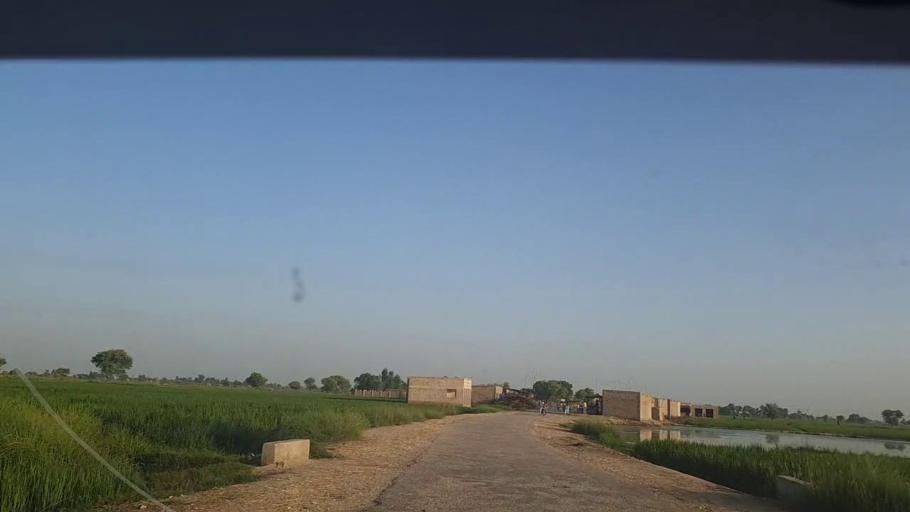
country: PK
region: Sindh
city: Thul
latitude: 28.1314
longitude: 68.8912
